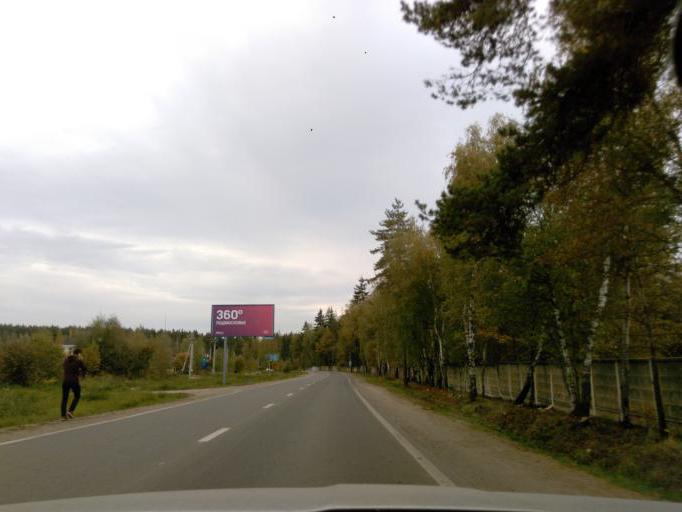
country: RU
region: Moskovskaya
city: Andreyevka
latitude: 55.9792
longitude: 37.1192
